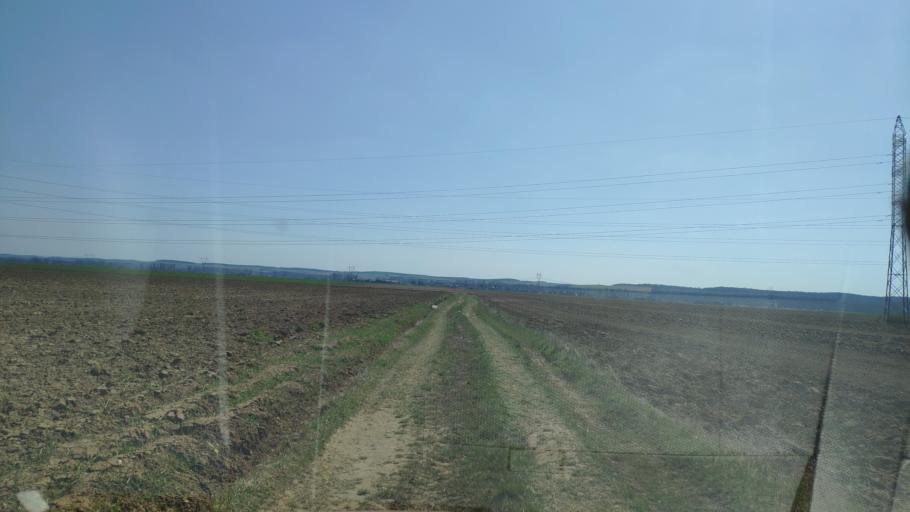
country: SK
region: Kosicky
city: Moldava nad Bodvou
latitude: 48.5995
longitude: 20.9453
